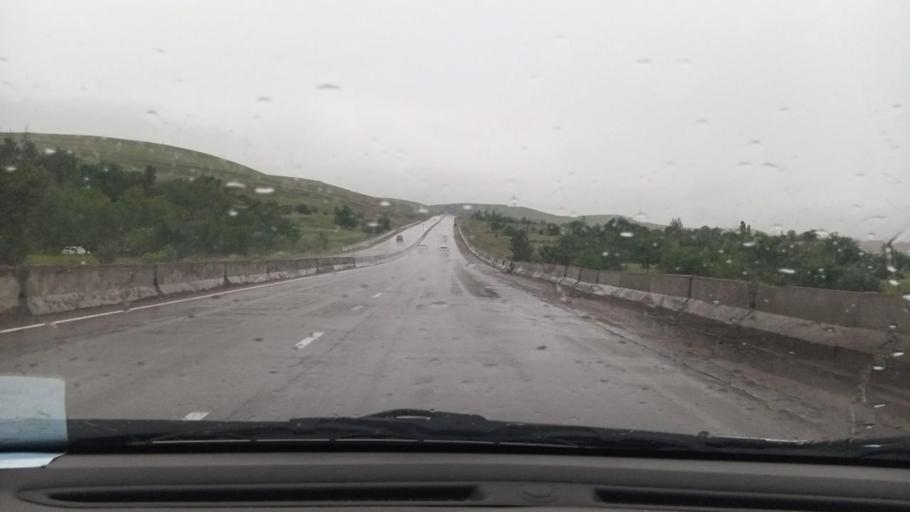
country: UZ
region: Toshkent
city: Angren
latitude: 41.0524
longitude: 70.1614
